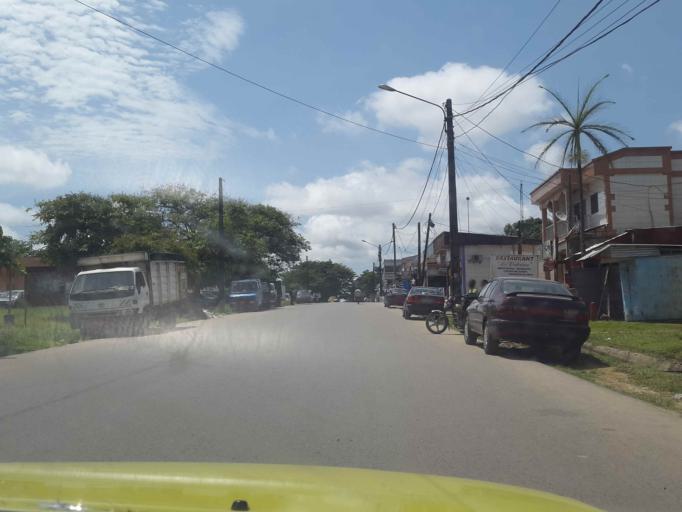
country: CM
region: Littoral
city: Douala
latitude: 4.0870
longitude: 9.7394
